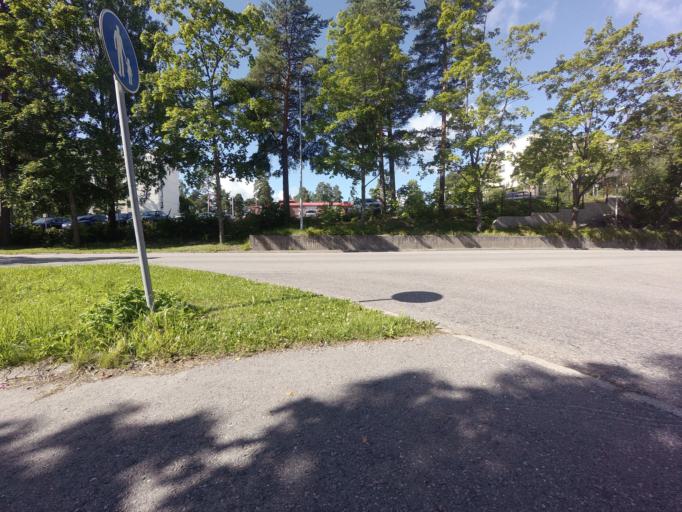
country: FI
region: Uusimaa
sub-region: Helsinki
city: Espoo
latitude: 60.1508
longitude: 24.6402
